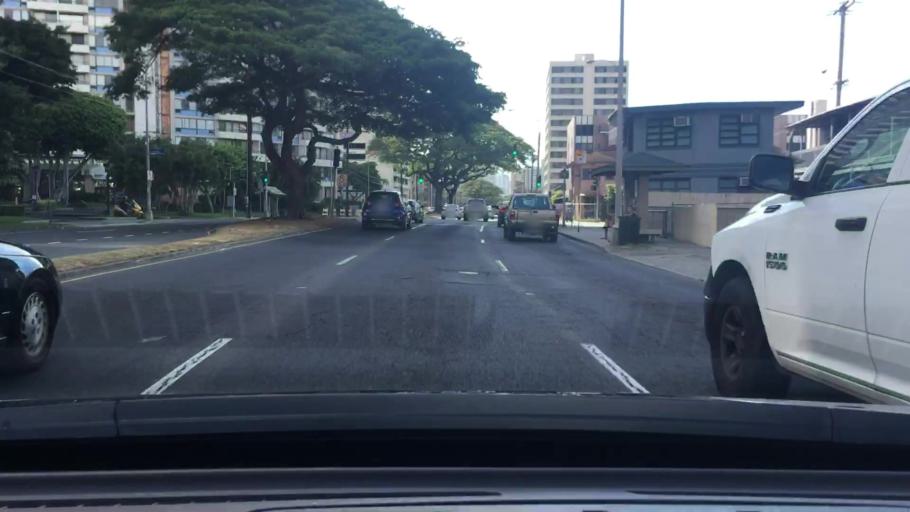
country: US
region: Hawaii
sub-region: Honolulu County
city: Honolulu
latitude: 21.2877
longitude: -157.8272
